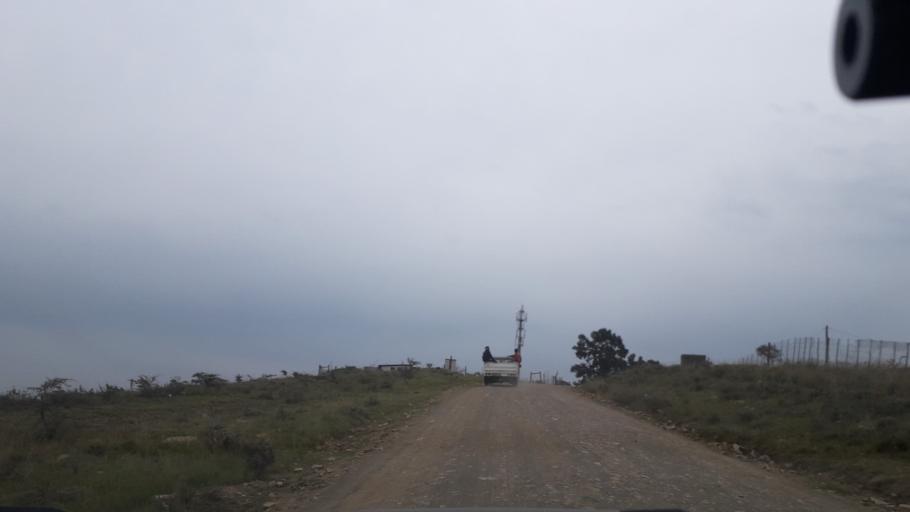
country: ZA
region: Eastern Cape
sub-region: Buffalo City Metropolitan Municipality
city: Bhisho
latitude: -32.7901
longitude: 27.3264
